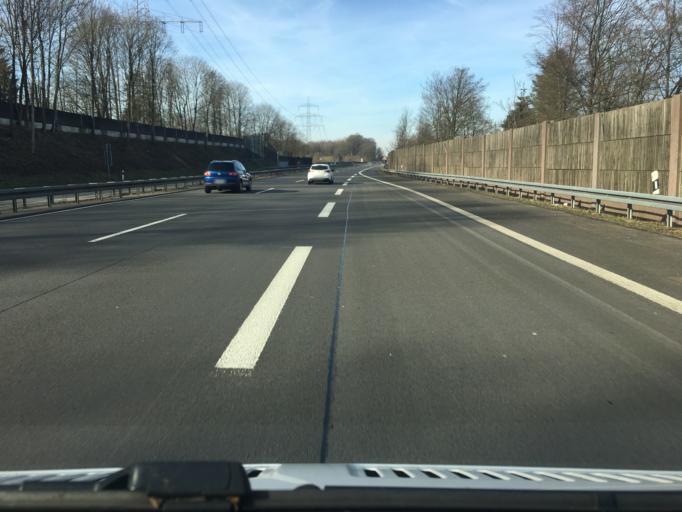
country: DE
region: North Rhine-Westphalia
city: Wiehl
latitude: 50.9733
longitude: 7.5203
